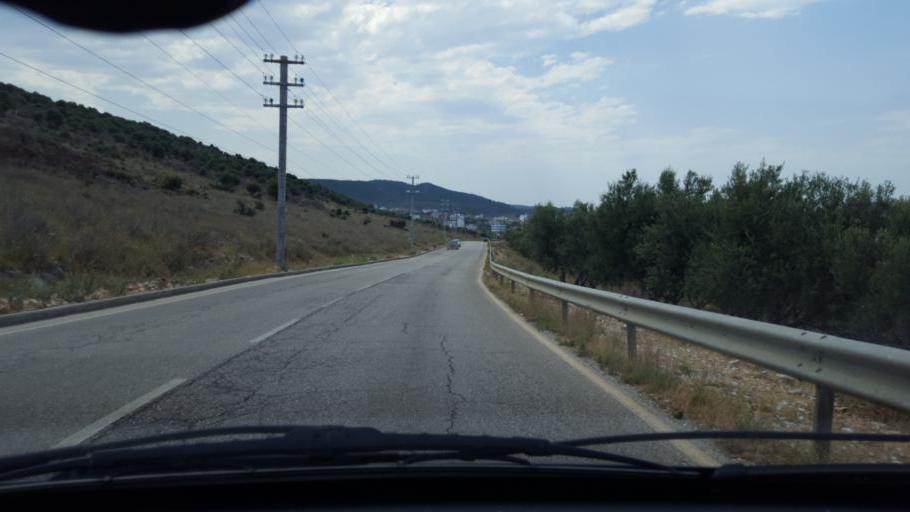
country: AL
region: Vlore
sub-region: Rrethi i Sarandes
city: Xarre
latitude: 39.7868
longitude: 20.0073
